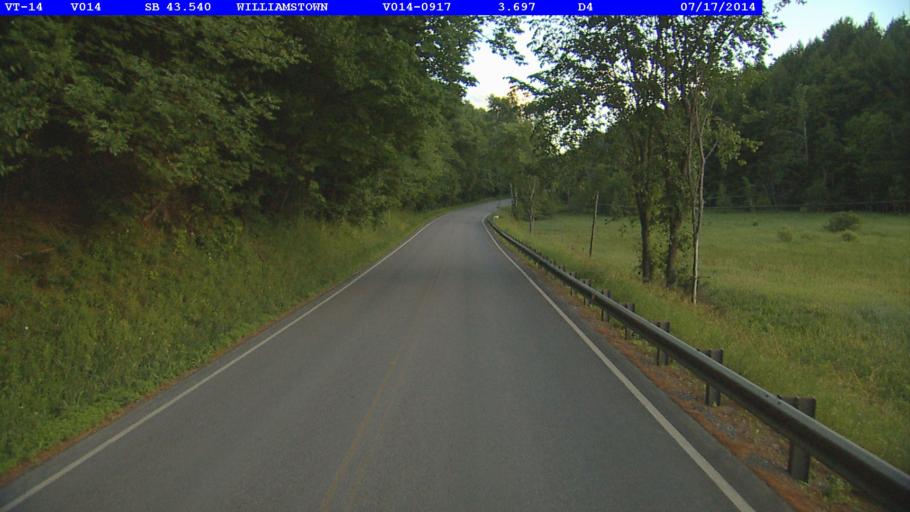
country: US
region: Vermont
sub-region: Orange County
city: Williamstown
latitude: 44.1110
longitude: -72.5402
